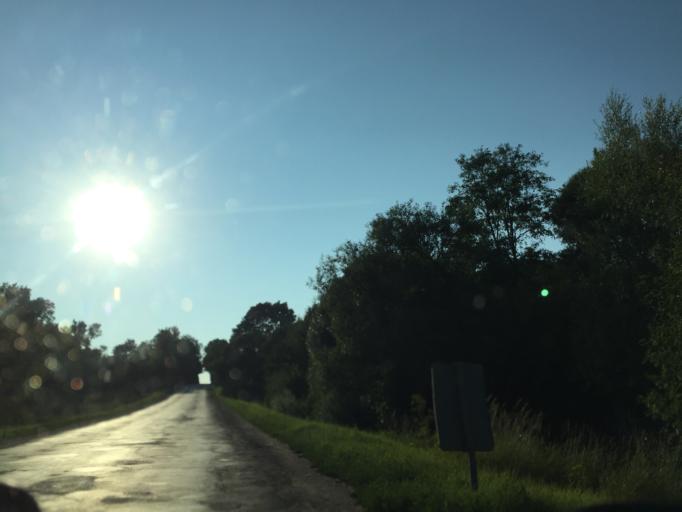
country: LV
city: Tervete
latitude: 56.4338
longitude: 23.5291
